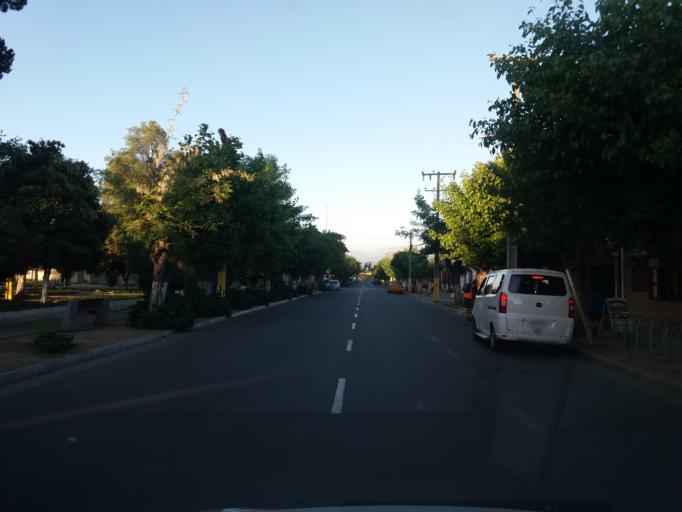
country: CL
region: Valparaiso
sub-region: Provincia de Quillota
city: Quillota
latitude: -32.9384
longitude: -71.2764
